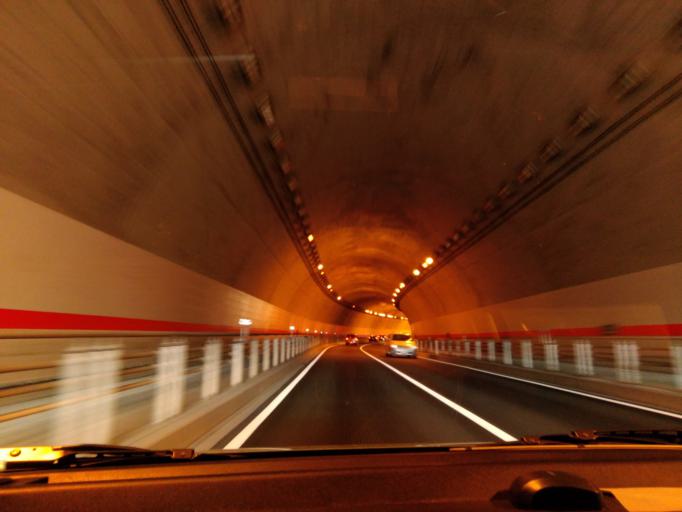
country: JP
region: Akita
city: Akita
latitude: 39.7438
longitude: 140.1351
